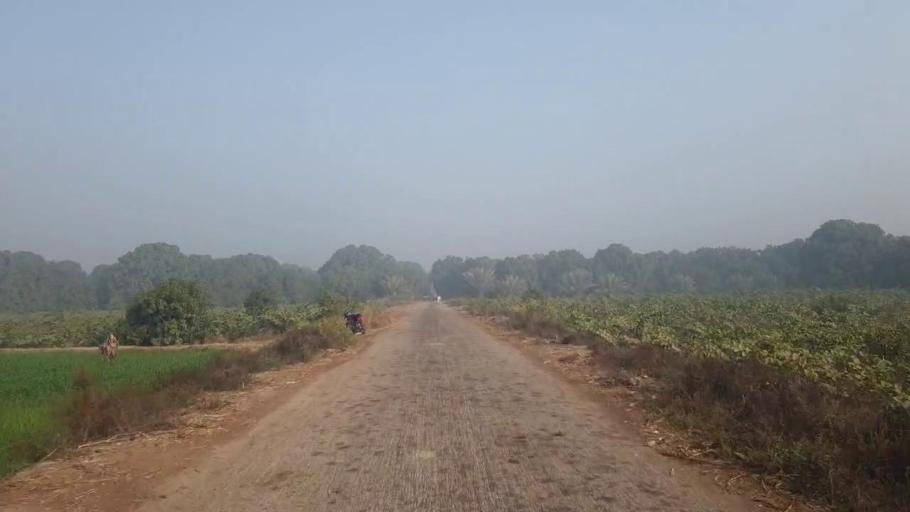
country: PK
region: Sindh
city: Tando Adam
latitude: 25.7929
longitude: 68.6334
